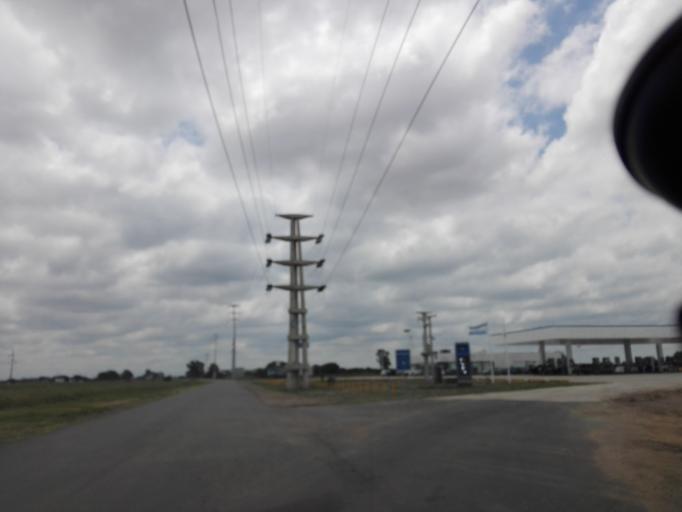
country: AR
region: Cordoba
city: Pilar
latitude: -31.6534
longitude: -63.8540
